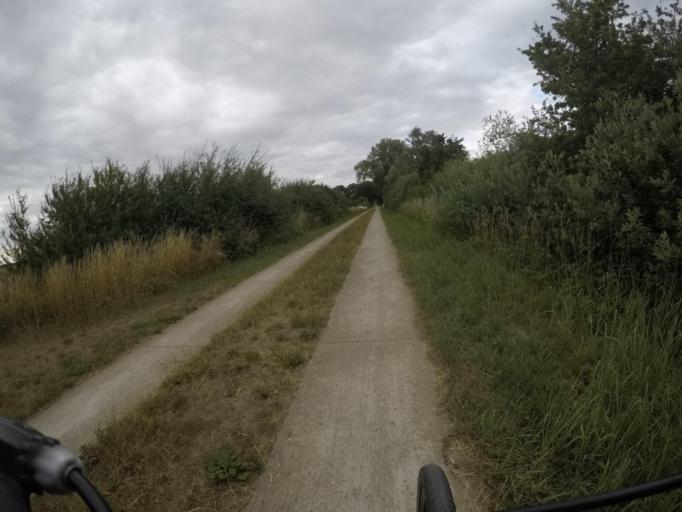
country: DE
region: Lower Saxony
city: Neu Darchau
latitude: 53.2542
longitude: 10.9170
